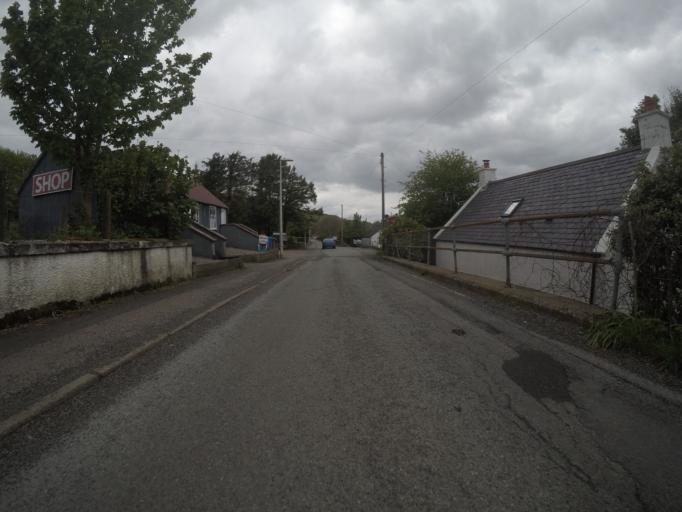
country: GB
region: Scotland
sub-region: Highland
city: Isle of Skye
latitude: 57.3008
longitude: -6.3513
